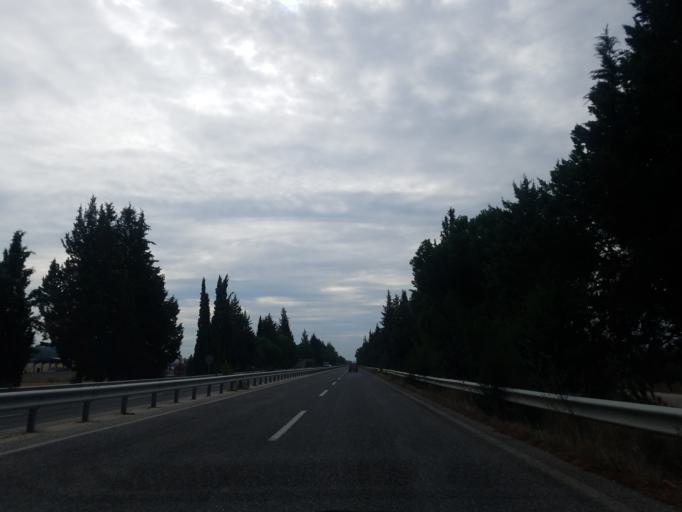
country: GR
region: Thessaly
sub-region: Trikala
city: Vasiliki
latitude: 39.6511
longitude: 21.6838
